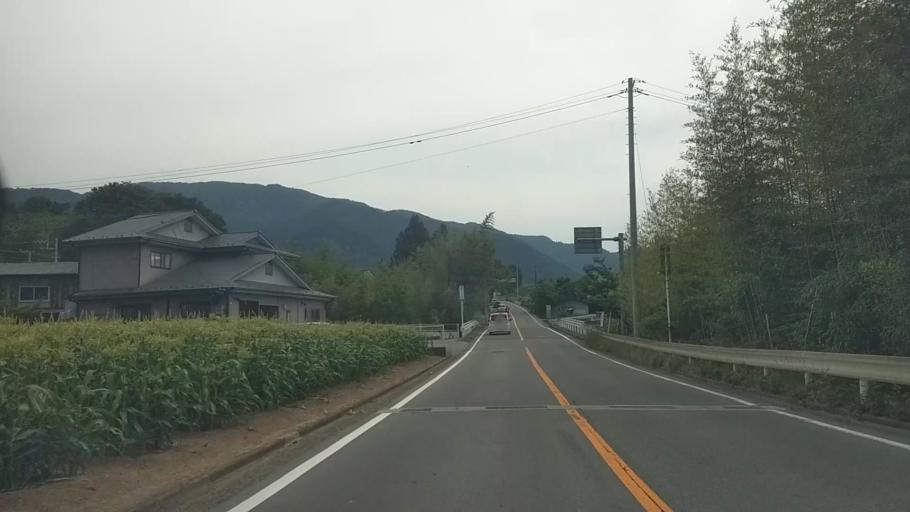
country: JP
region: Yamanashi
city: Isawa
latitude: 35.5763
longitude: 138.5925
